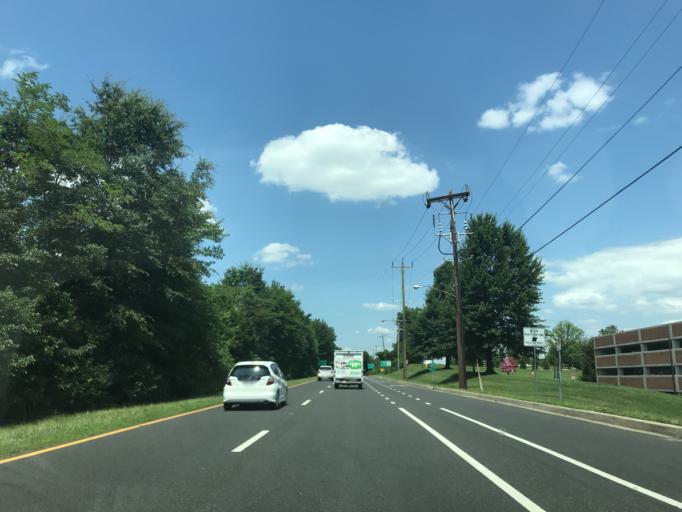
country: US
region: Maryland
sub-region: Prince George's County
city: College Park
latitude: 38.9867
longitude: -76.9555
